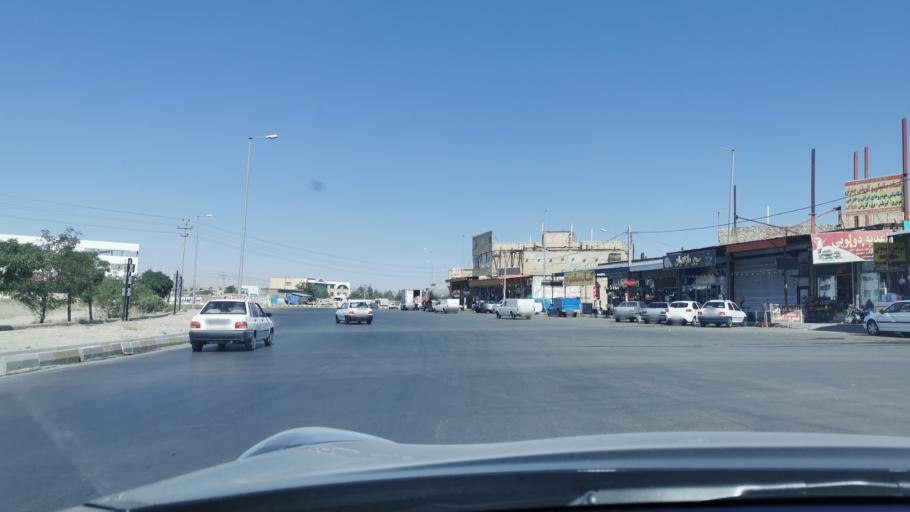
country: IR
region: Razavi Khorasan
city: Chenaran
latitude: 36.6347
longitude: 59.1313
